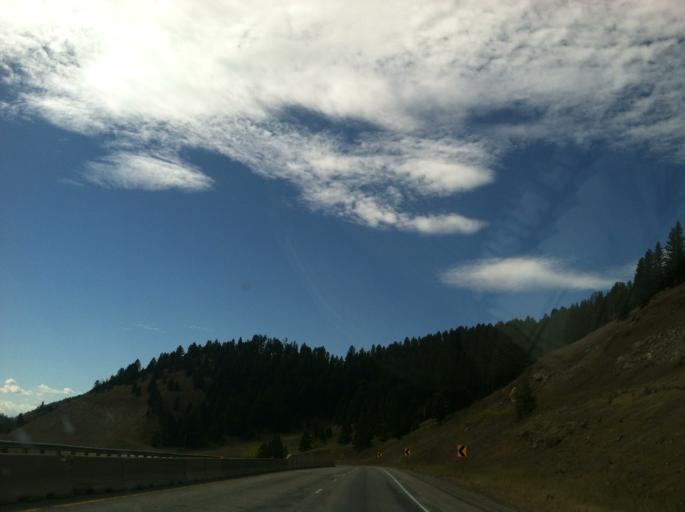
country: US
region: Montana
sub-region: Gallatin County
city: Bozeman
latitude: 45.6486
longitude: -110.8690
